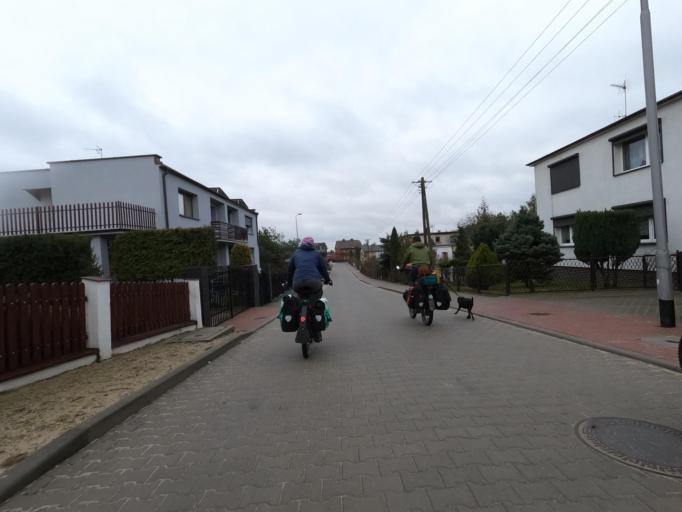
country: PL
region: Greater Poland Voivodeship
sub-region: Powiat pilski
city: Osiek nad Notecia
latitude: 53.1215
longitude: 17.2982
